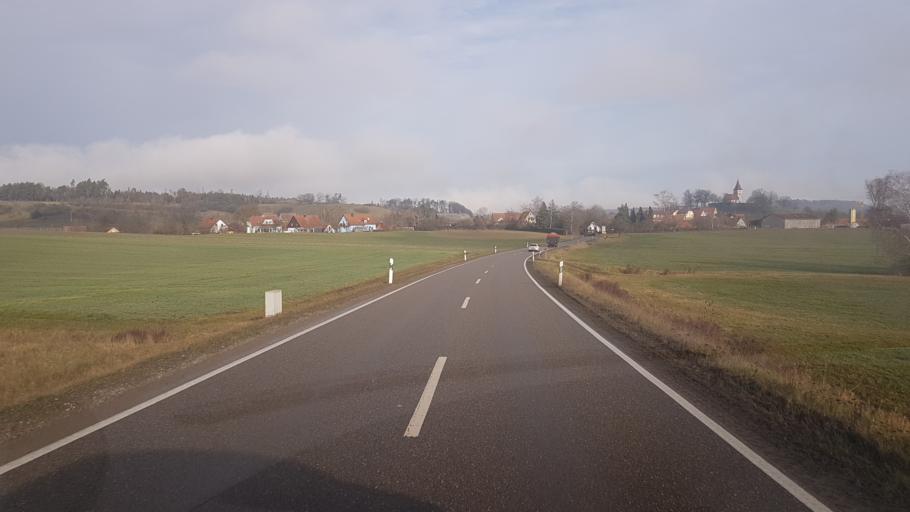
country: DE
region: Bavaria
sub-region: Regierungsbezirk Mittelfranken
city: Dombuhl
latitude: 49.2509
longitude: 10.2782
